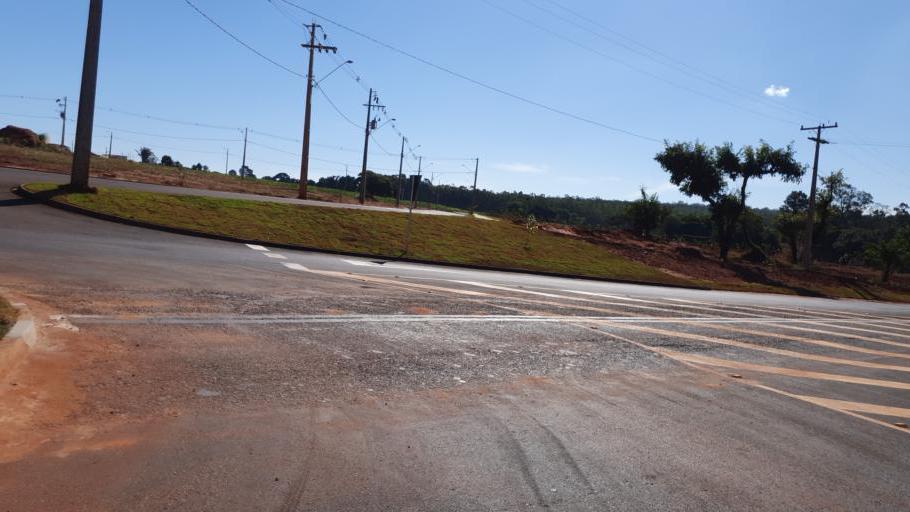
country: BR
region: Sao Paulo
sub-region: Paraguacu Paulista
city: Paraguacu Paulista
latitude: -22.3977
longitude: -50.5740
